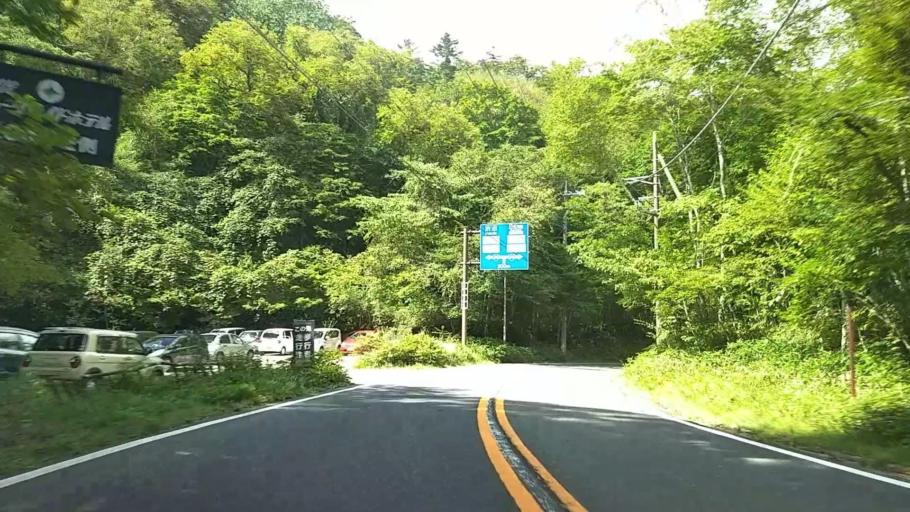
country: JP
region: Tochigi
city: Nikko
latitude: 36.7357
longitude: 139.4996
